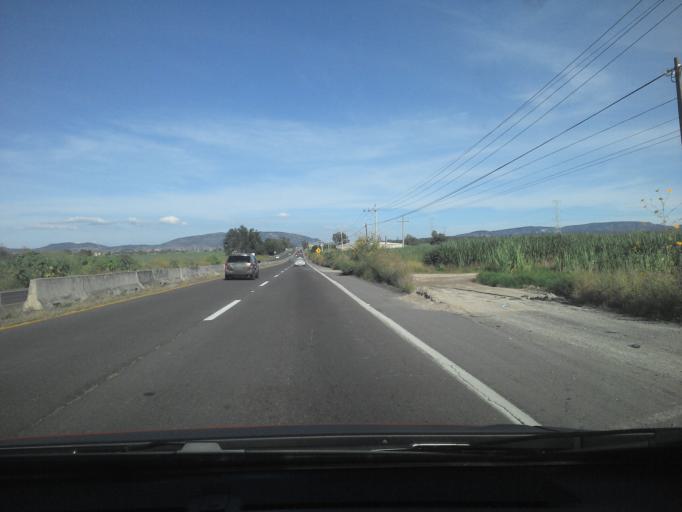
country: MX
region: Jalisco
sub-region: Tala
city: Los Ruisenores
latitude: 20.7063
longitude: -103.6801
